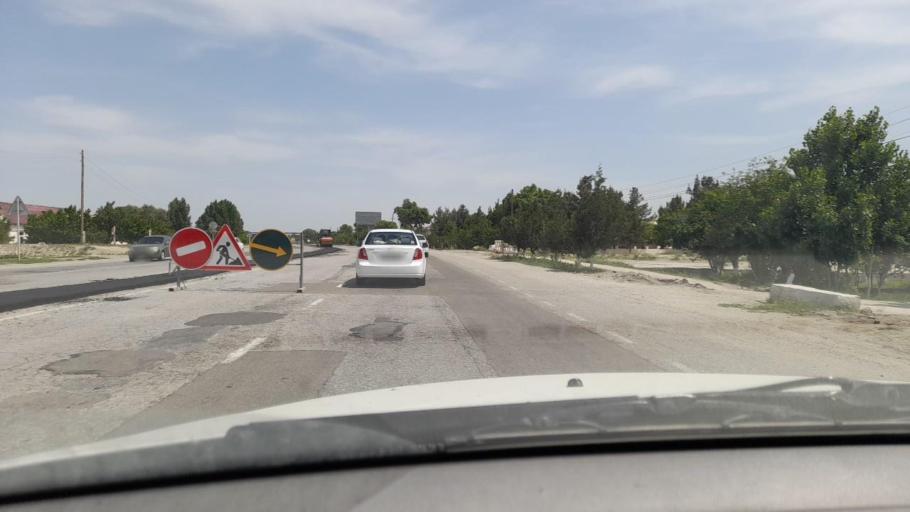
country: UZ
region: Navoiy
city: Beshrabot
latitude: 40.1382
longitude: 65.2793
